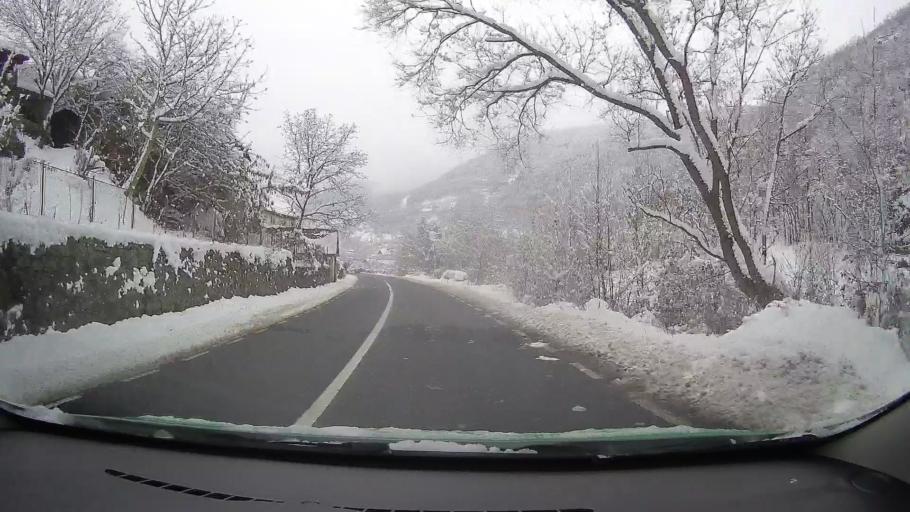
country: RO
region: Alba
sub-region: Comuna Sasciori
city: Sasciori
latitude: 45.8469
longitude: 23.6018
